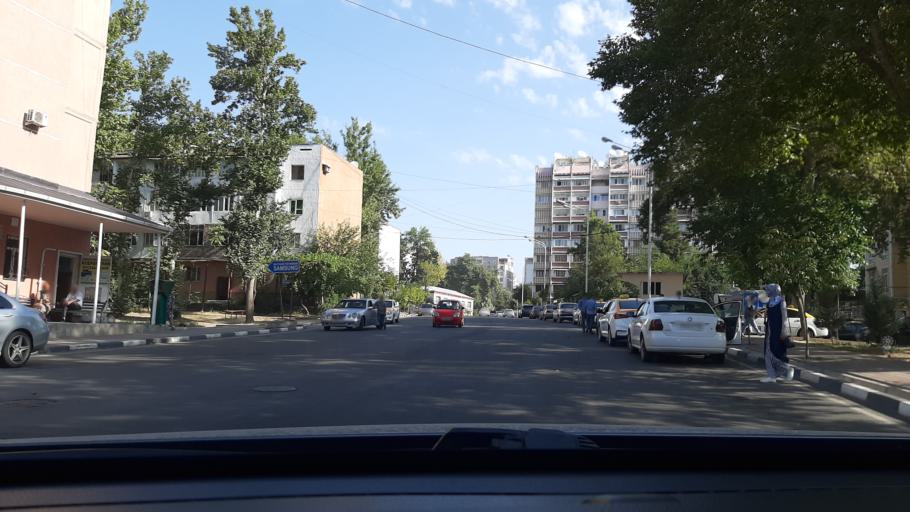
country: TJ
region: Dushanbe
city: Dushanbe
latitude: 38.5840
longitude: 68.7451
